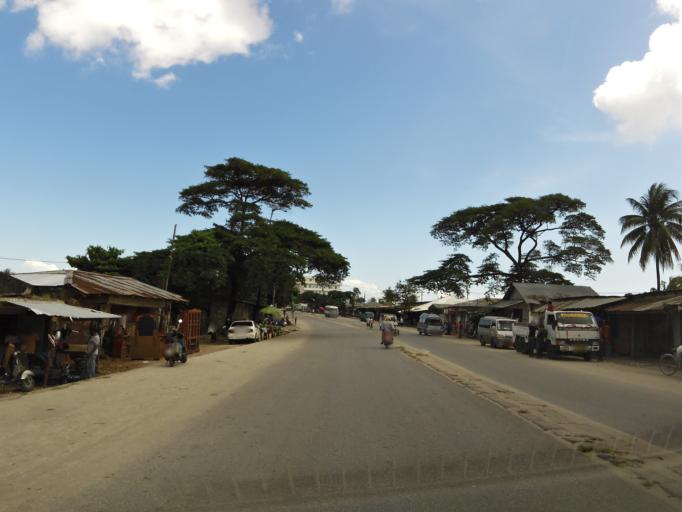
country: TZ
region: Zanzibar Urban/West
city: Zanzibar
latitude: -6.1634
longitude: 39.2178
